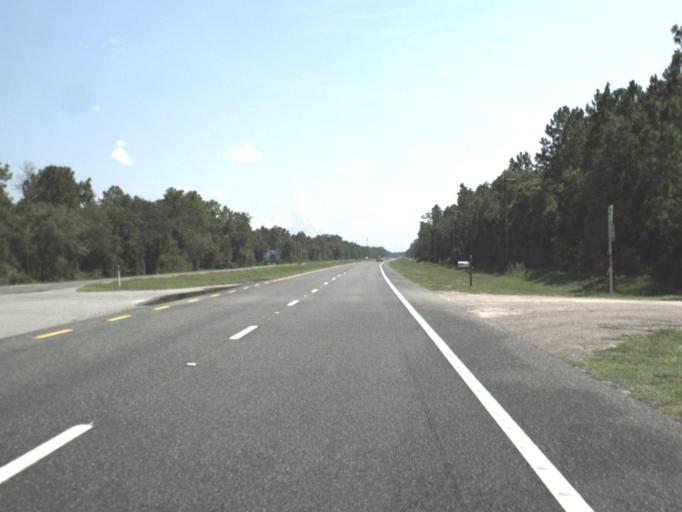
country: US
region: Florida
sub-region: Levy County
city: Inglis
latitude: 29.1331
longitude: -82.6372
